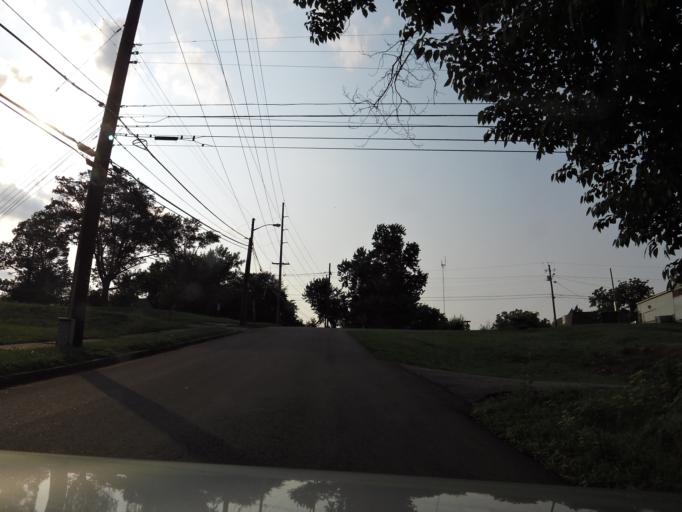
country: US
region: Tennessee
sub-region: Knox County
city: Knoxville
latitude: 35.9800
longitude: -83.9445
